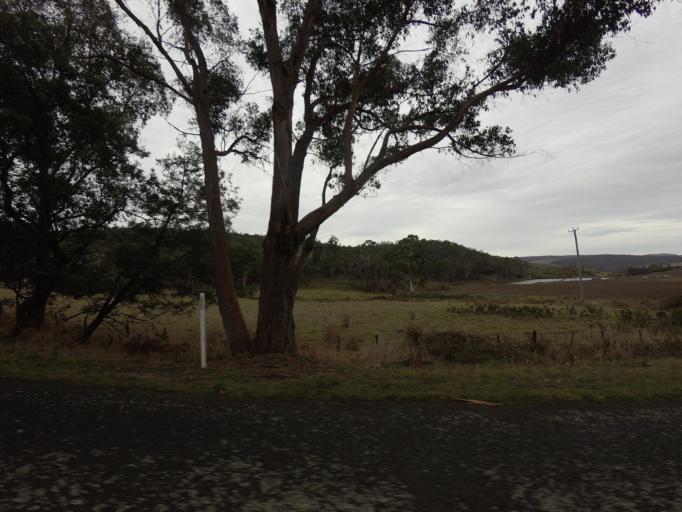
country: AU
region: Tasmania
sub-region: Derwent Valley
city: New Norfolk
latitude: -42.5978
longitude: 147.0492
